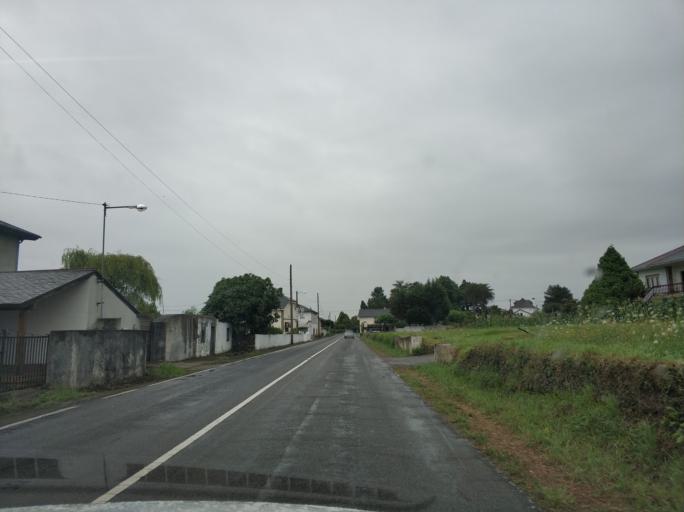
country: ES
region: Asturias
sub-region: Province of Asturias
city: Navia
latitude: 43.5335
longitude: -6.5269
